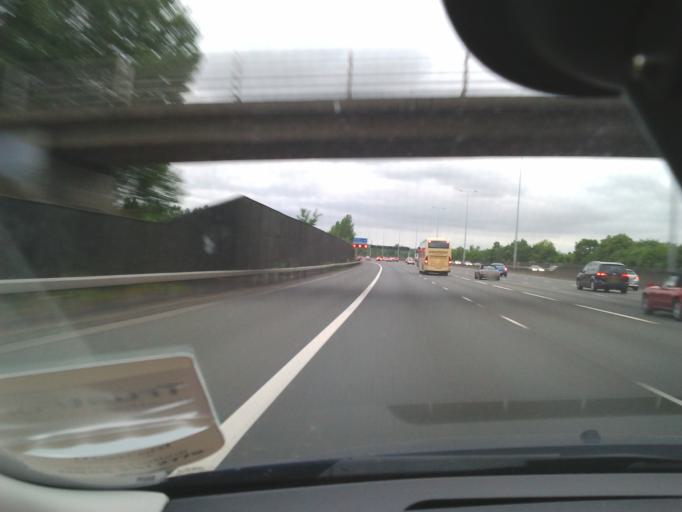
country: GB
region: England
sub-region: Surrey
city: Egham
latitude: 51.4139
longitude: -0.5402
